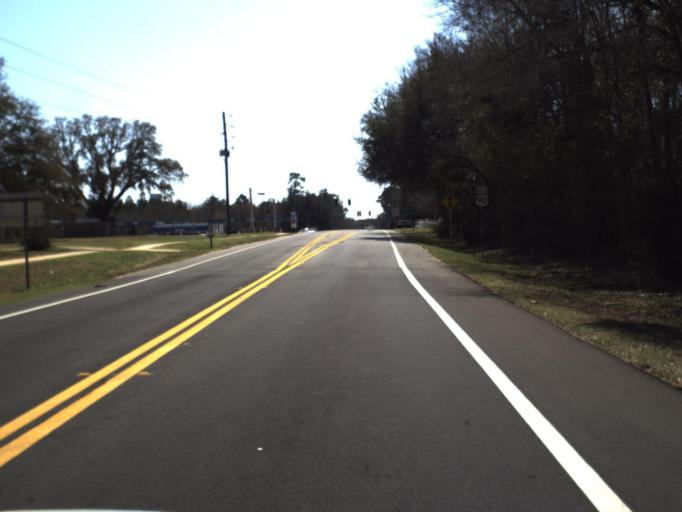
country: US
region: Florida
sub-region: Jackson County
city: Sneads
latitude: 30.7213
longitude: -85.0202
